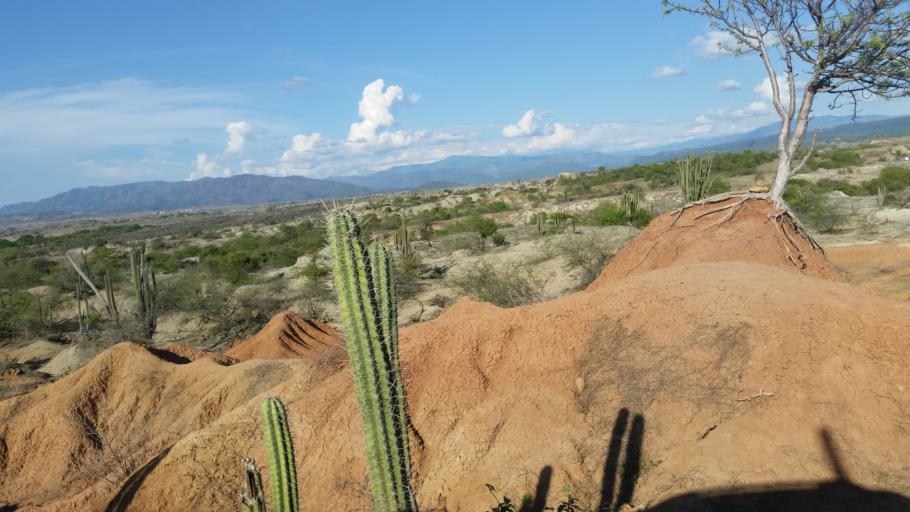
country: CO
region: Huila
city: Villavieja
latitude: 3.2281
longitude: -75.1506
